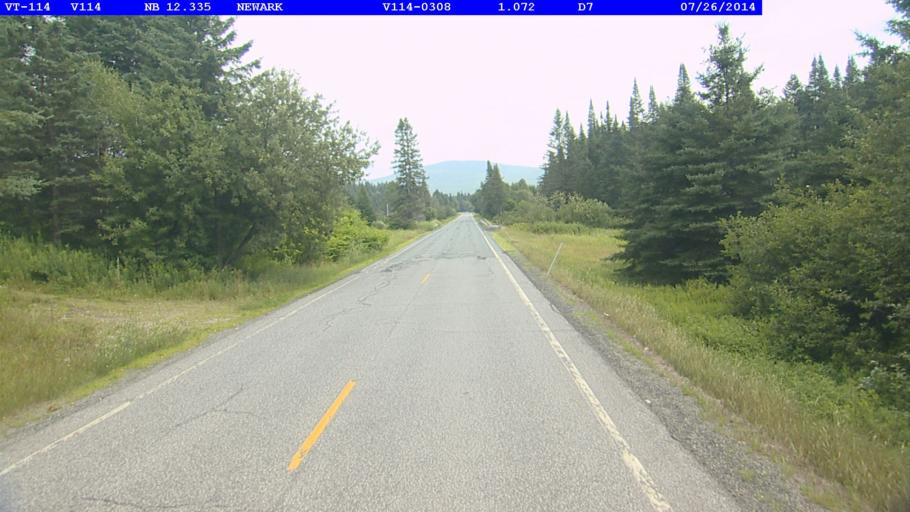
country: US
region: Vermont
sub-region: Caledonia County
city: Lyndonville
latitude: 44.6842
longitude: -71.8784
